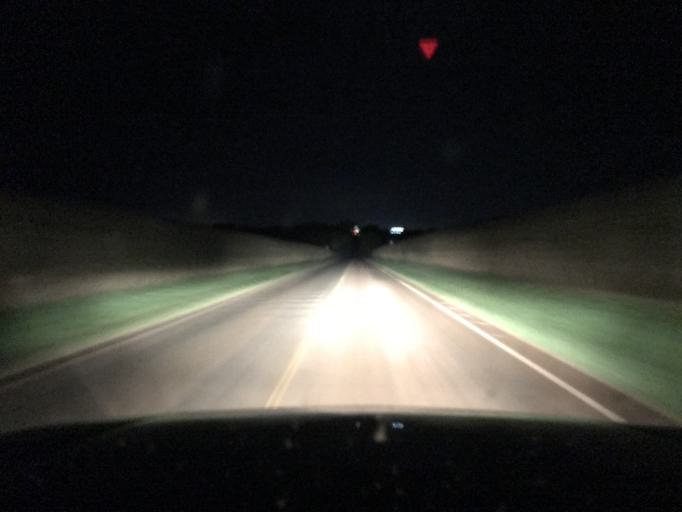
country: BR
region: Parana
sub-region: Palotina
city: Palotina
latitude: -24.2486
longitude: -53.8442
